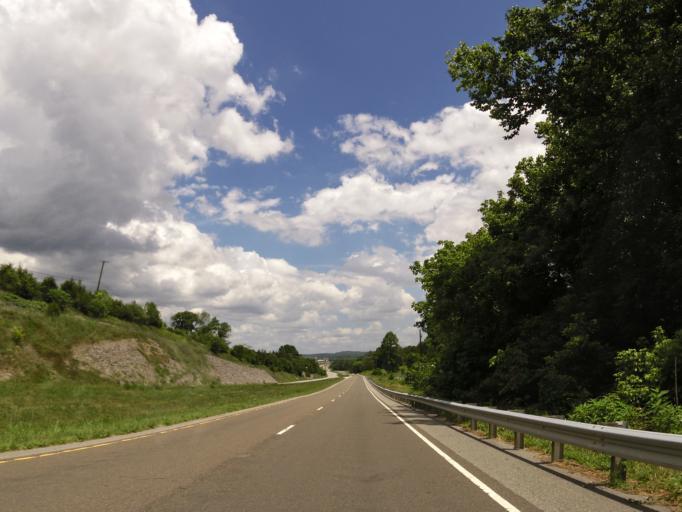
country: US
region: Tennessee
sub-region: Claiborne County
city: Harrogate
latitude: 36.6047
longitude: -83.6131
